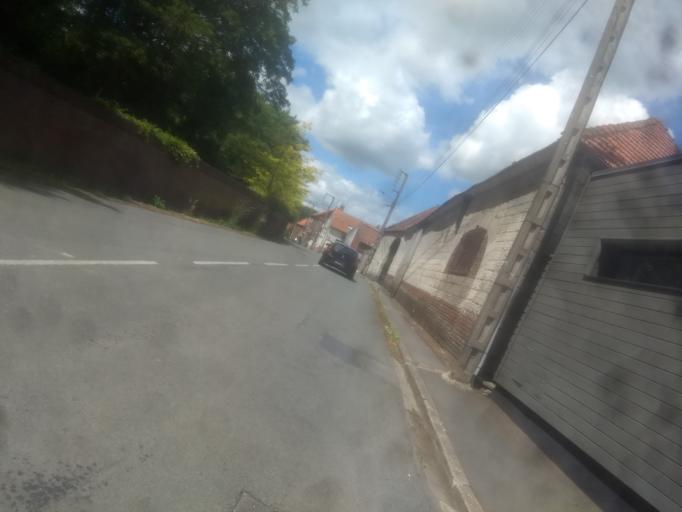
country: FR
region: Nord-Pas-de-Calais
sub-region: Departement du Pas-de-Calais
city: Maroeuil
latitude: 50.3120
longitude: 2.7187
